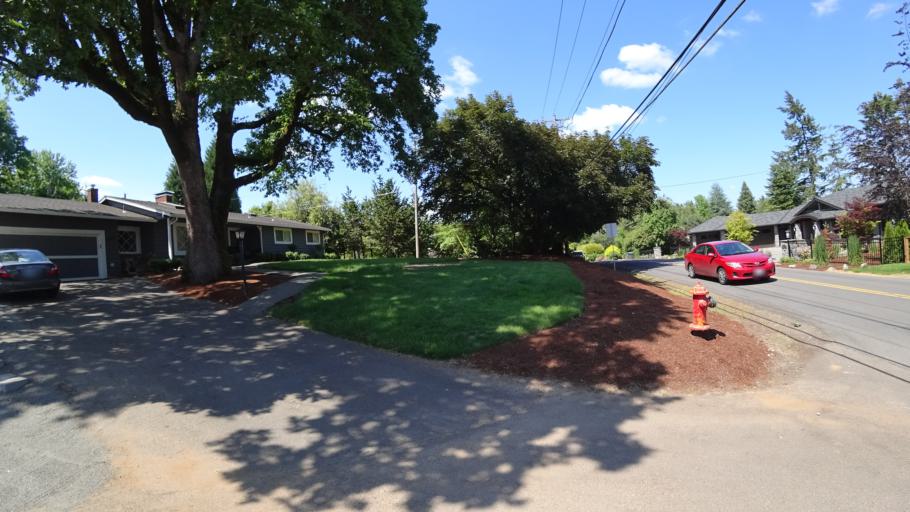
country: US
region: Oregon
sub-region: Clackamas County
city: Lake Oswego
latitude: 45.4272
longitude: -122.6924
